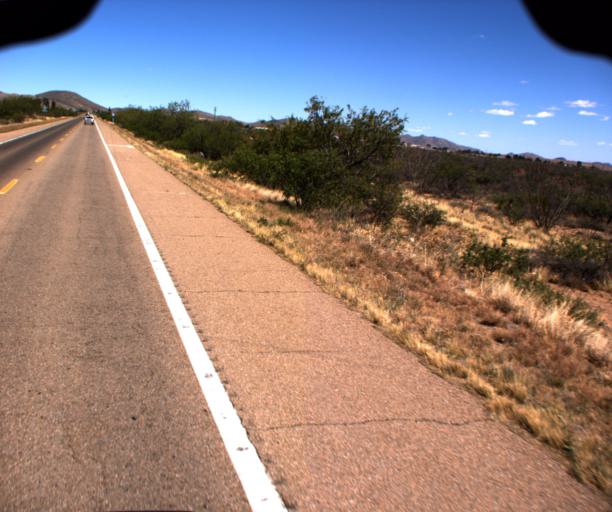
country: US
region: Arizona
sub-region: Cochise County
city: Naco
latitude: 31.3895
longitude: -109.9428
